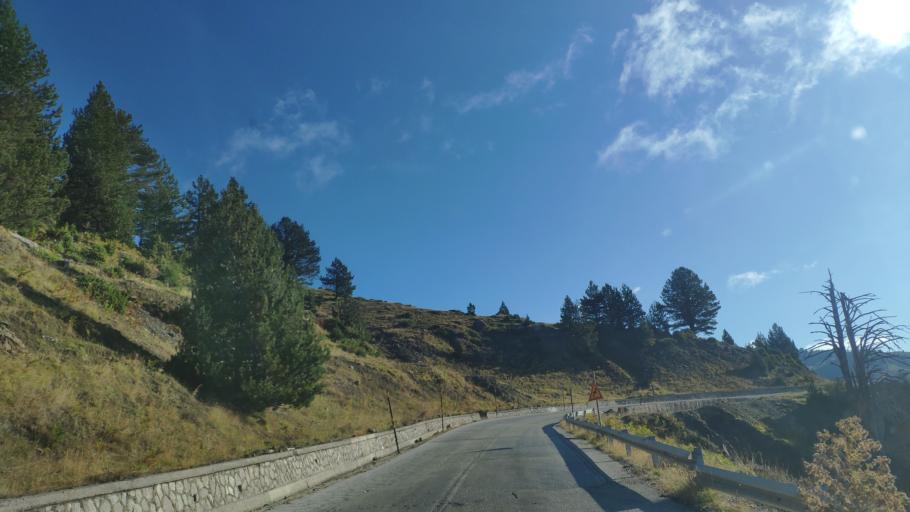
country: GR
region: Epirus
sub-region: Nomos Ioanninon
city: Metsovo
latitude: 39.7979
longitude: 21.1701
